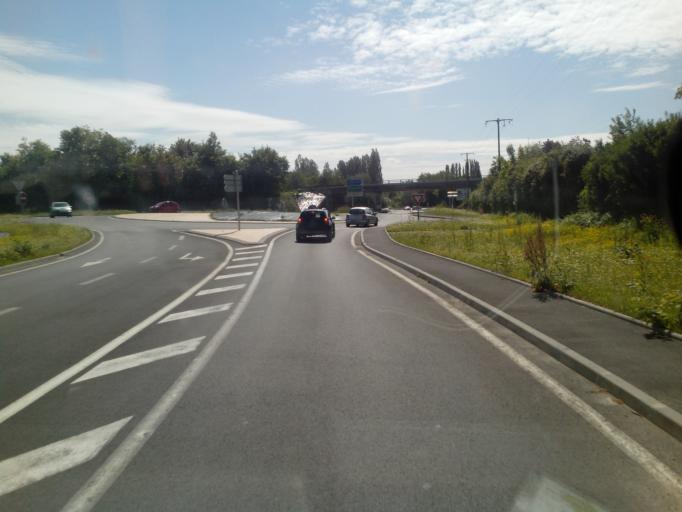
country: FR
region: Lower Normandy
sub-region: Departement du Calvados
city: Saint-Gatien-des-Bois
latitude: 49.2952
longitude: 0.1993
